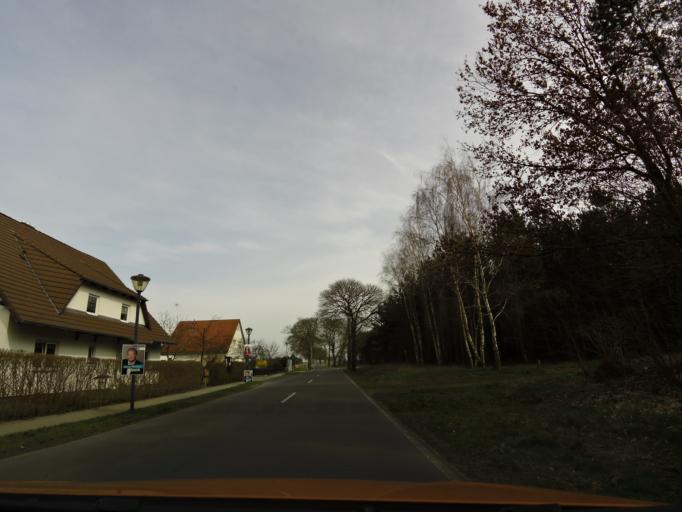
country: DE
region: Brandenburg
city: Ludwigsfelde
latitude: 52.3391
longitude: 13.2324
